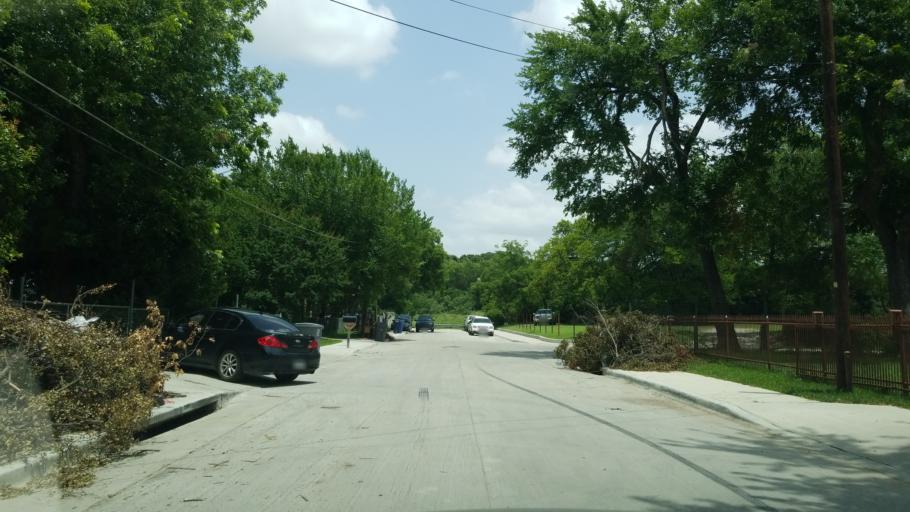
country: US
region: Texas
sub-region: Dallas County
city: Cockrell Hill
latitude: 32.7890
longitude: -96.8914
